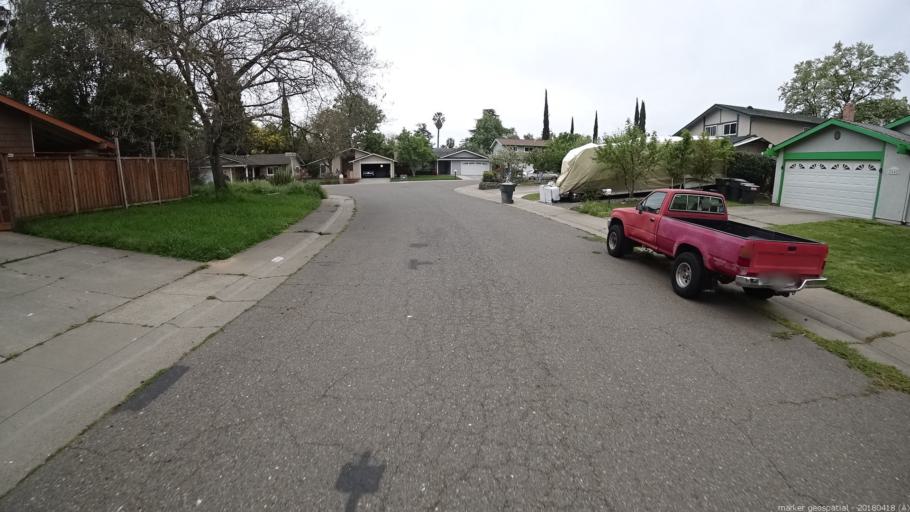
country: US
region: California
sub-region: Sacramento County
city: La Riviera
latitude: 38.5684
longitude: -121.3517
